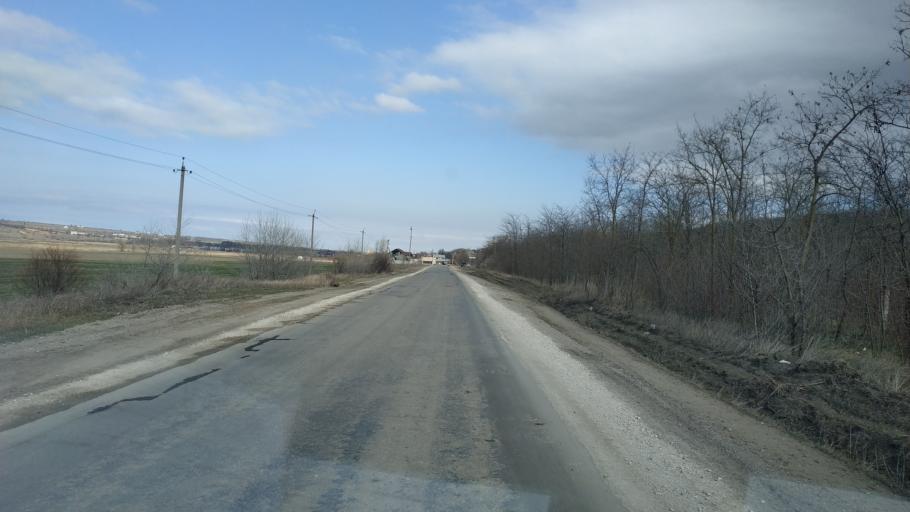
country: MD
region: Causeni
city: Causeni
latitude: 46.6384
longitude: 29.3796
